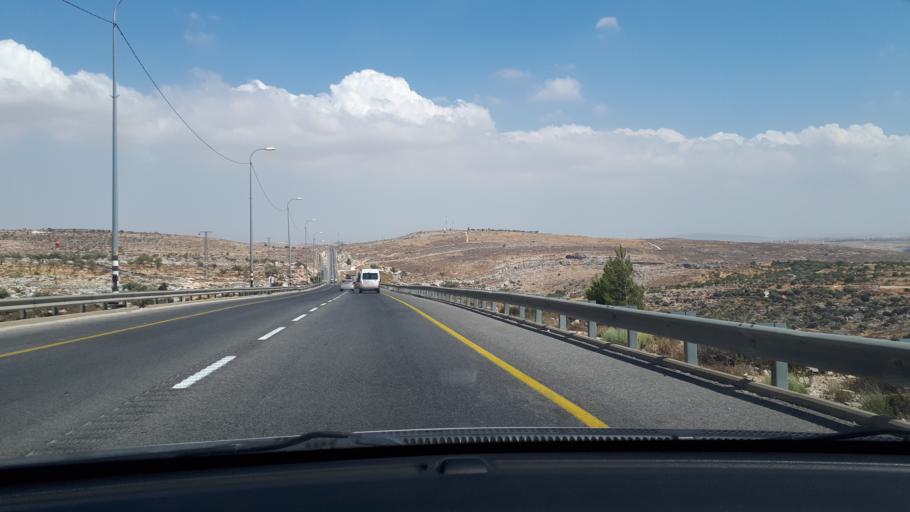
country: PS
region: West Bank
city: Burqah
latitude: 31.9022
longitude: 35.2597
